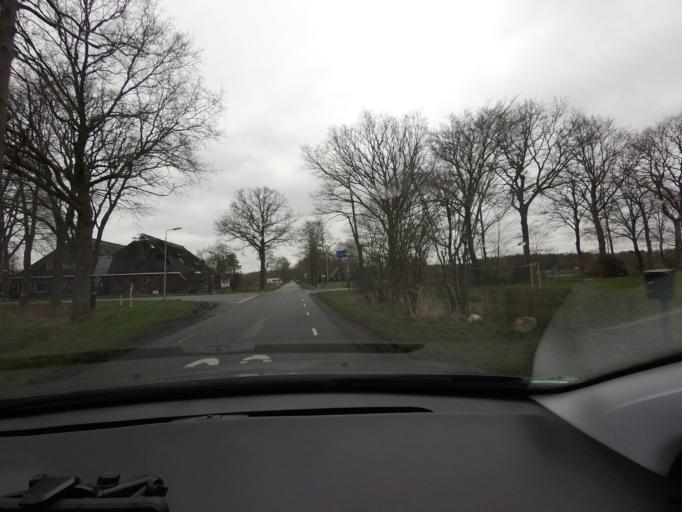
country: NL
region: Drenthe
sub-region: Gemeente Hoogeveen
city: Hoogeveen
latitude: 52.7705
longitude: 6.4945
